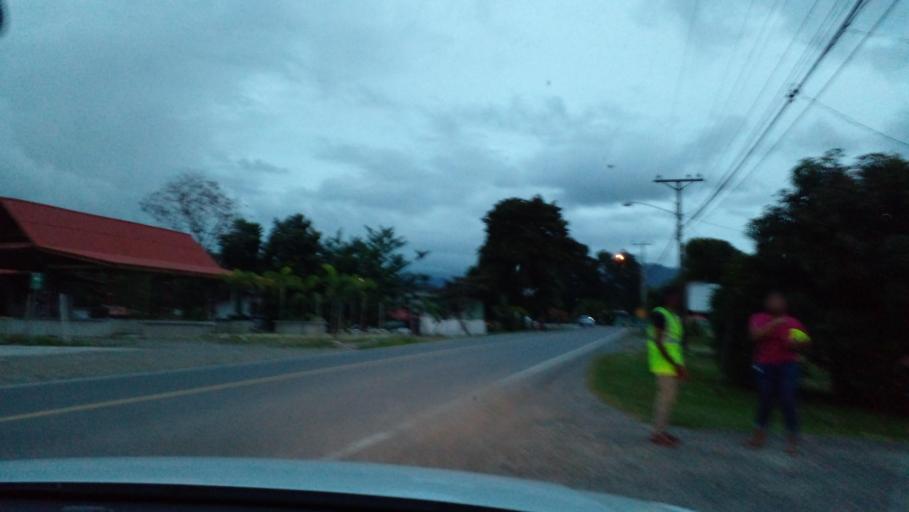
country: PA
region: Bocas del Toro
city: Chiriqui Grande
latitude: 8.9292
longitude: -82.1830
